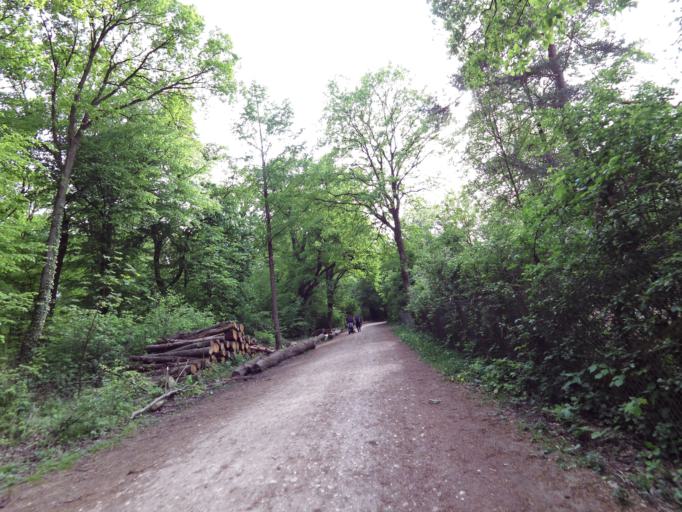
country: DE
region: North Rhine-Westphalia
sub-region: Regierungsbezirk Koln
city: Bonn
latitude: 50.6908
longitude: 7.0963
